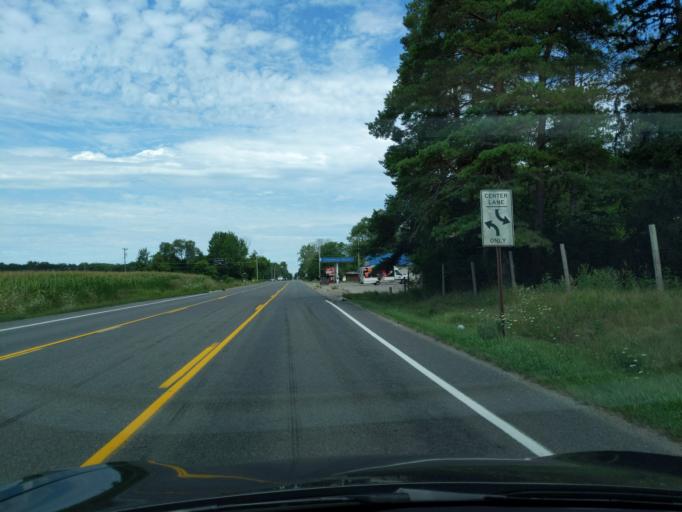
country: US
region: Michigan
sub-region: Midland County
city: Midland
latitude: 43.5659
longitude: -84.3696
